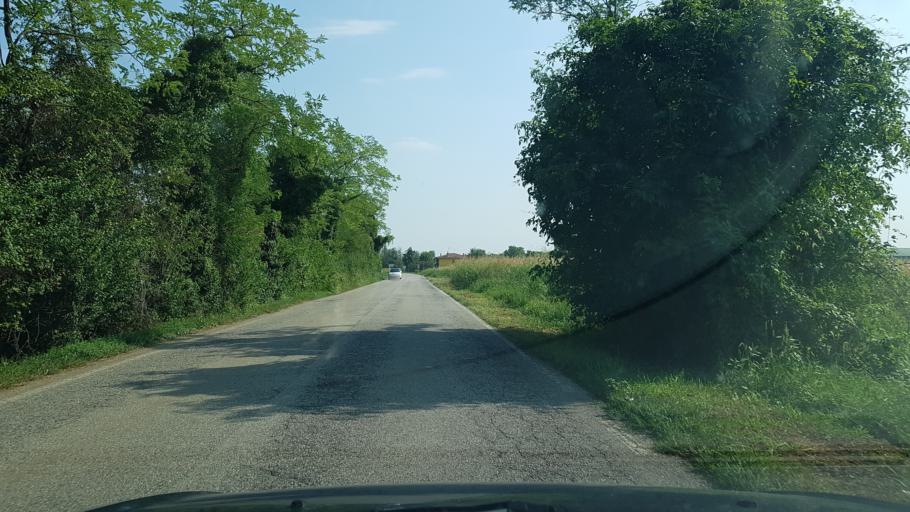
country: IT
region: Friuli Venezia Giulia
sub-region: Provincia di Udine
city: San Vito di Fagagna
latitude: 46.0767
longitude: 13.0762
